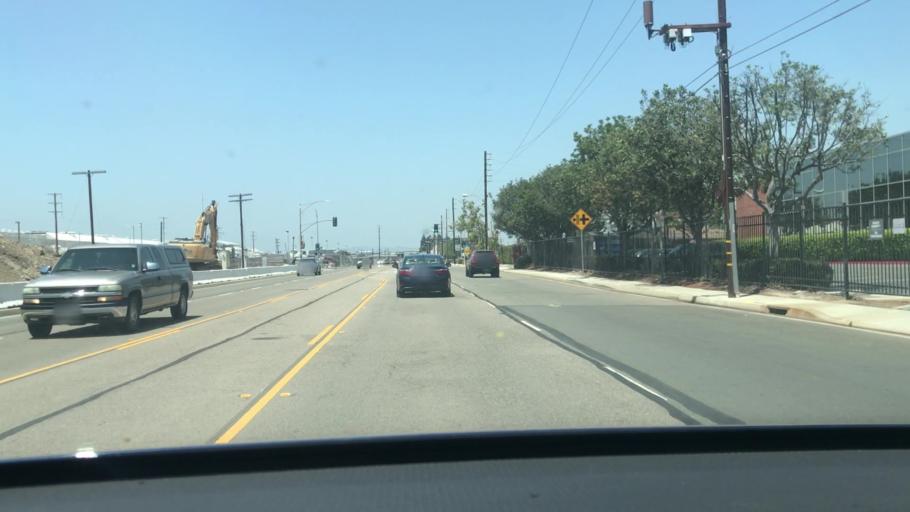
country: US
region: California
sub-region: Los Angeles County
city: Del Aire
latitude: 33.9192
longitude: -118.3784
